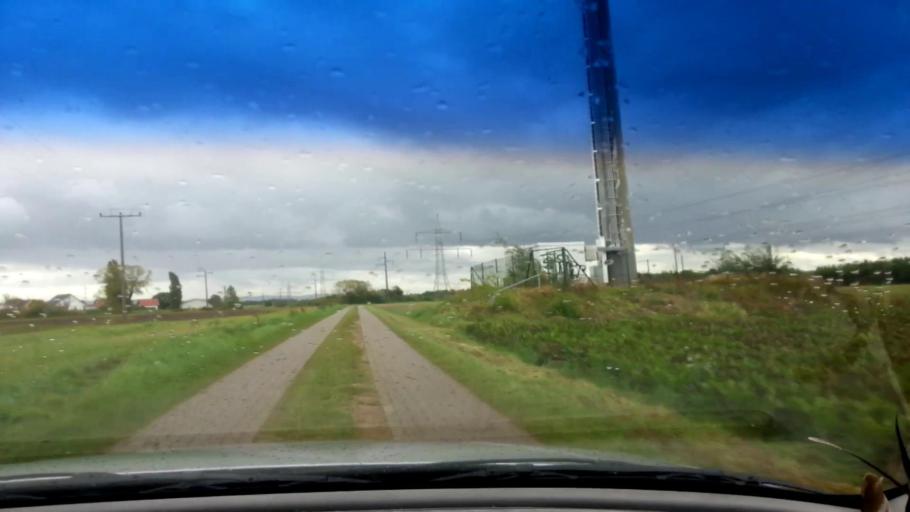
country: DE
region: Bavaria
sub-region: Upper Franconia
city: Oberhaid
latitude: 49.9288
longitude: 10.8099
